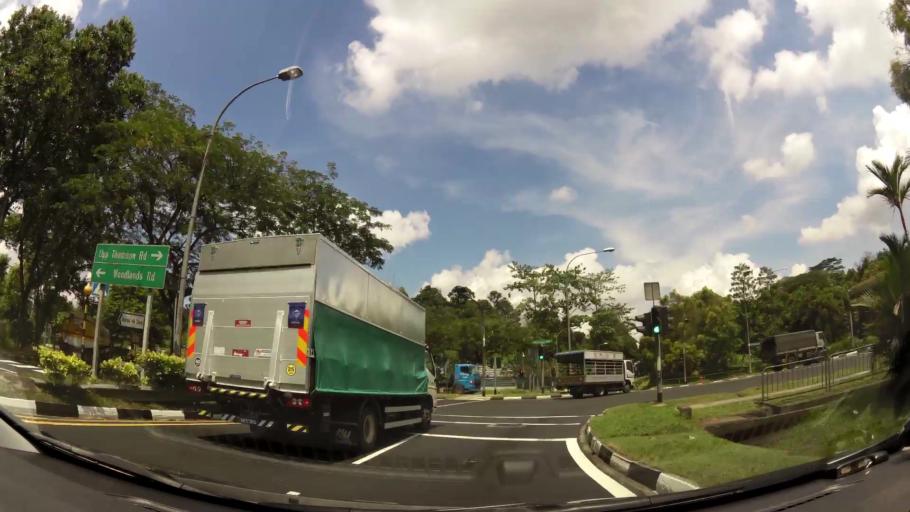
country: MY
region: Johor
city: Johor Bahru
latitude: 1.4099
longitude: 103.7711
